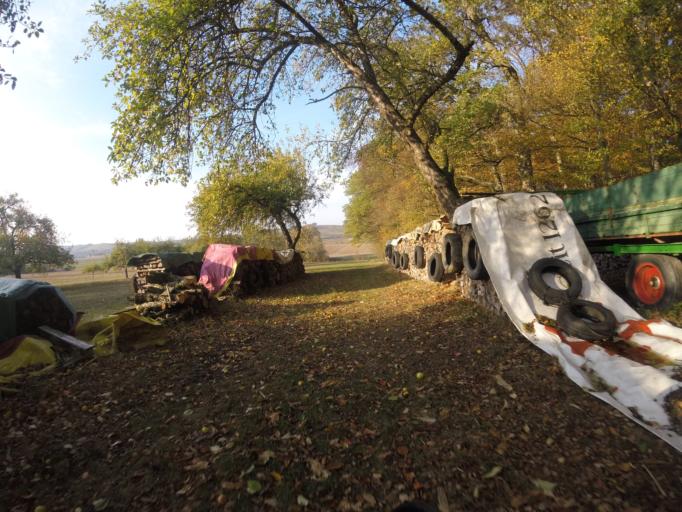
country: DE
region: Baden-Wuerttemberg
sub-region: Regierungsbezirk Stuttgart
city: Aspach
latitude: 48.9845
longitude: 9.3844
